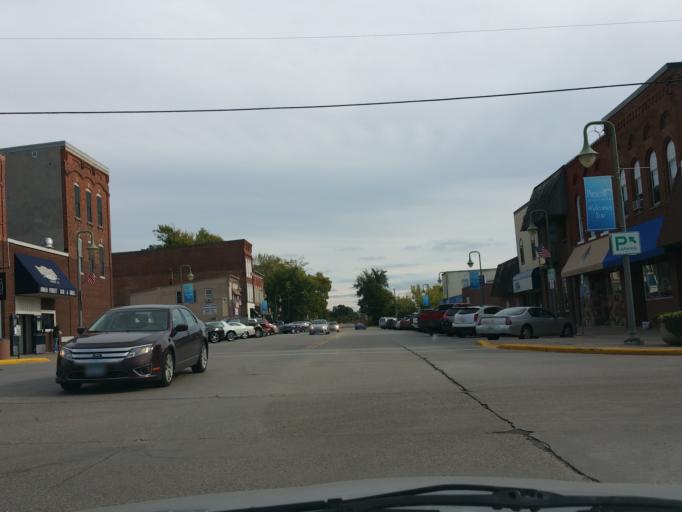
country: US
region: Wisconsin
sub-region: Pierce County
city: Prescott
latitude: 44.7488
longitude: -92.8019
